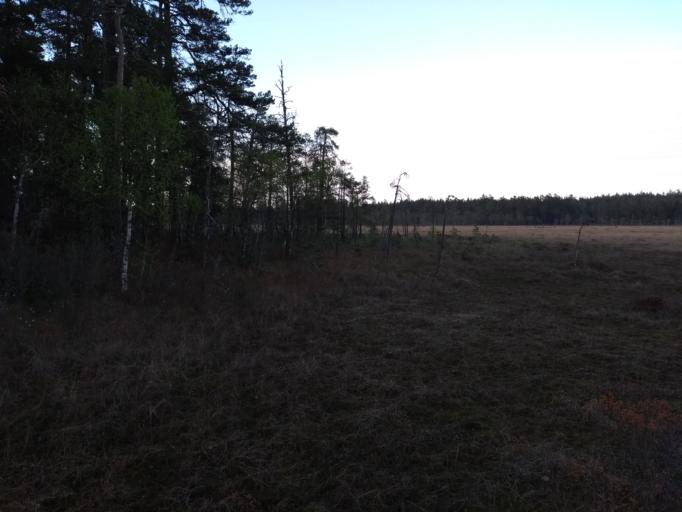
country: SE
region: Soedermanland
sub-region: Nykopings Kommun
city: Olstorp
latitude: 58.6911
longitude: 16.5518
